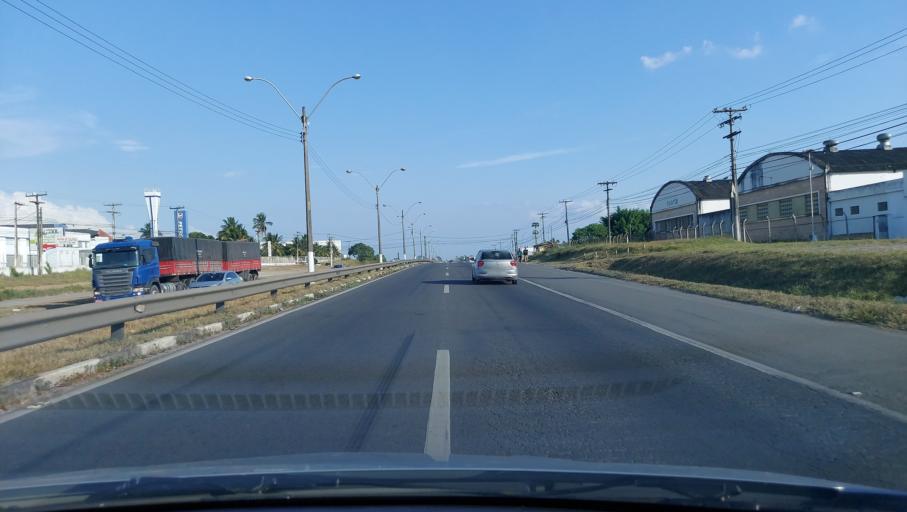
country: BR
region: Bahia
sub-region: Feira De Santana
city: Feira de Santana
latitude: -12.2811
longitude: -38.9239
